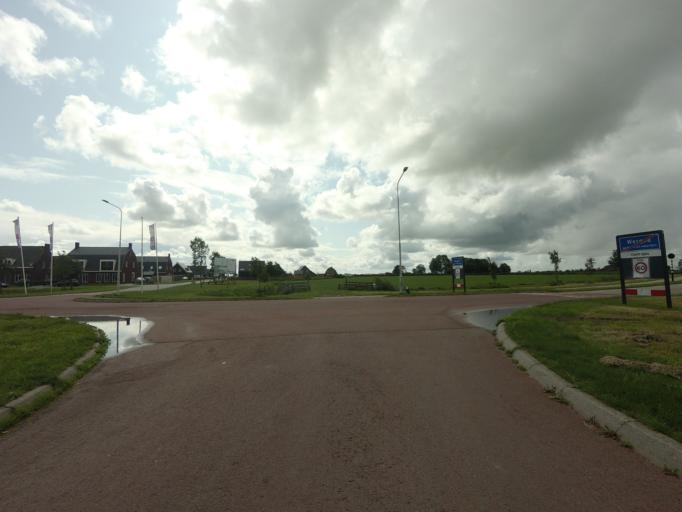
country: NL
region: Friesland
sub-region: Gemeente Boarnsterhim
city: Wergea
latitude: 53.1512
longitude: 5.8374
